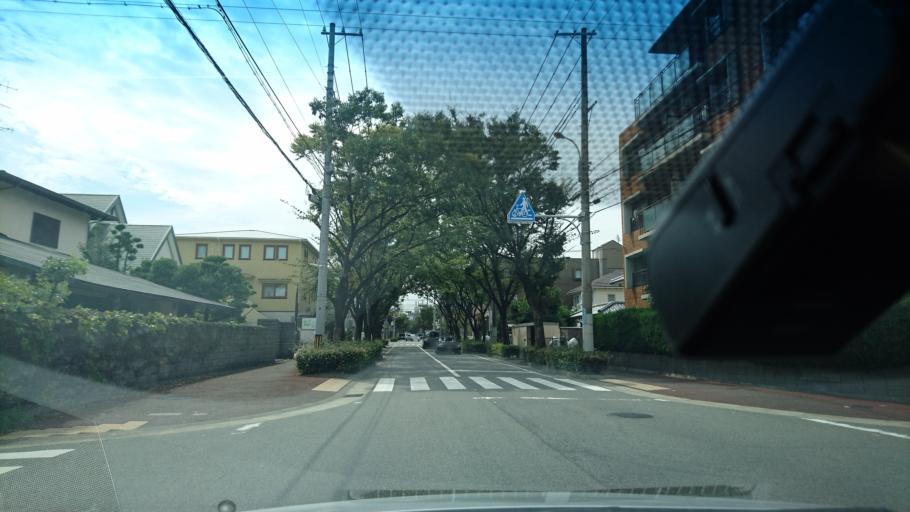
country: JP
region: Hyogo
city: Ashiya
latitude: 34.7309
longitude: 135.3114
